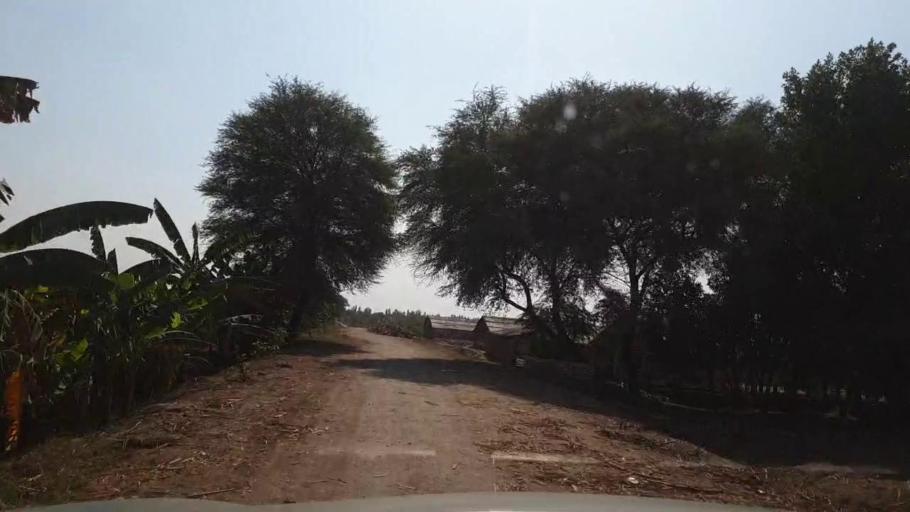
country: PK
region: Sindh
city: Tando Allahyar
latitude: 25.5481
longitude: 68.6981
